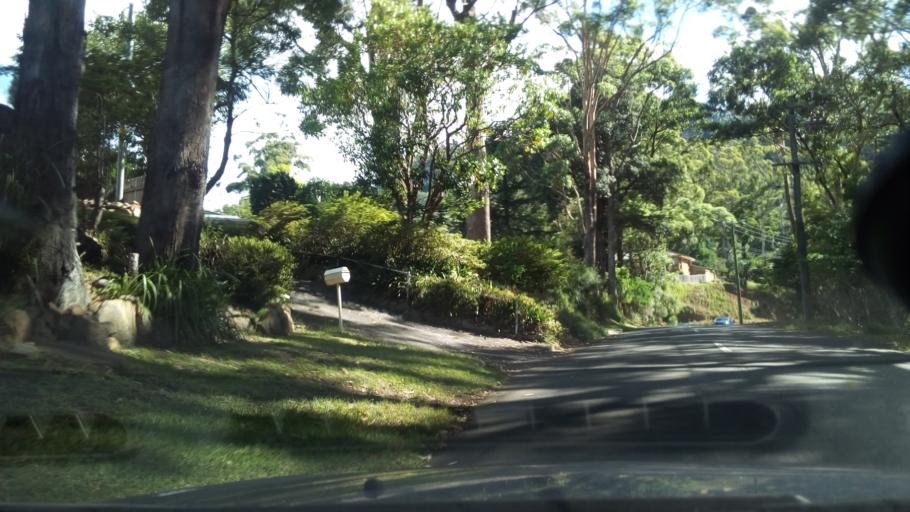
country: AU
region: New South Wales
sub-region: Wollongong
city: Mount Ousley
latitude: -34.3954
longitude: 150.8628
